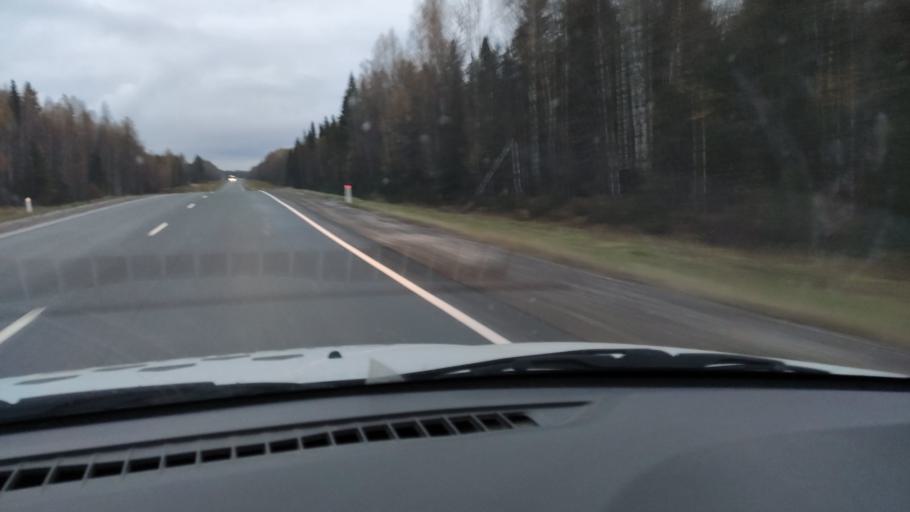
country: RU
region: Kirov
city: Kostino
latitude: 58.8467
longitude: 53.0843
